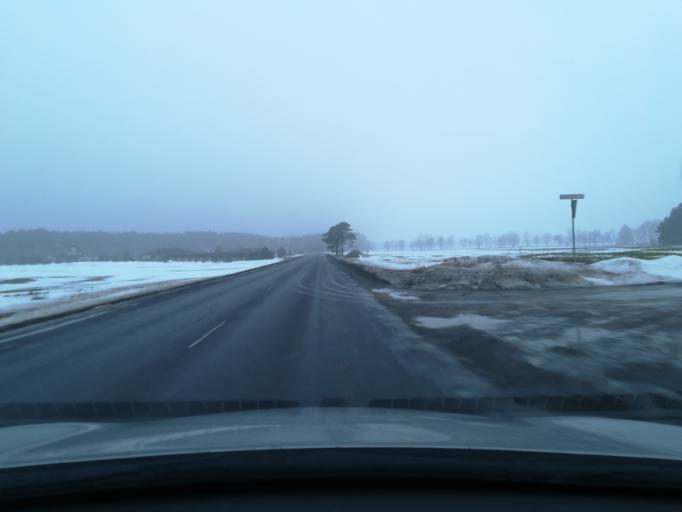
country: EE
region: Harju
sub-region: Raasiku vald
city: Arukula
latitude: 59.3527
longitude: 25.0822
